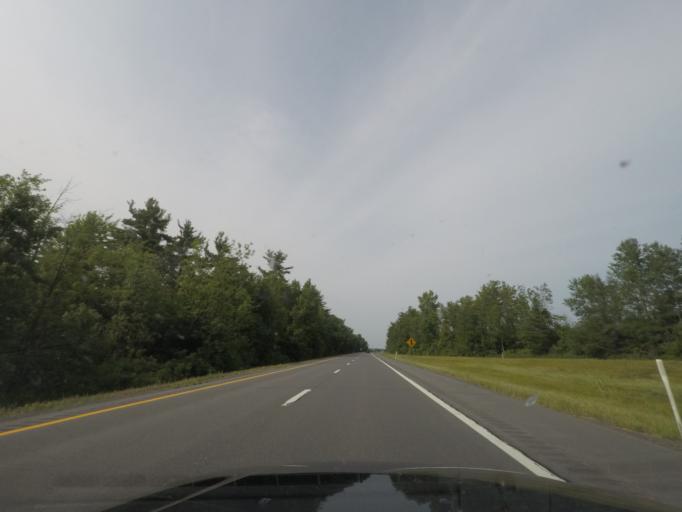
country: US
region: New York
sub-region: Clinton County
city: Peru
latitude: 44.5798
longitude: -73.5021
